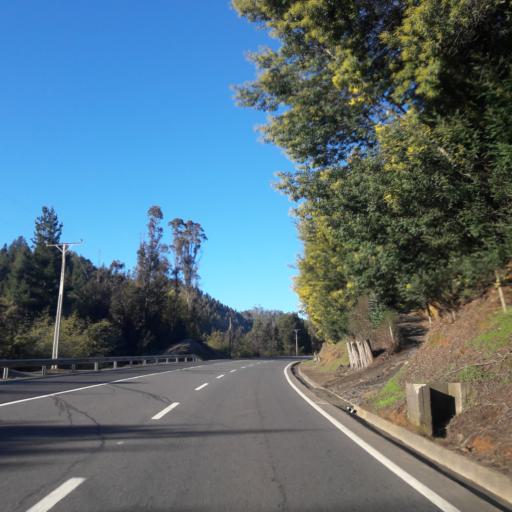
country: CL
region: Biobio
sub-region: Provincia de Biobio
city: La Laja
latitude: -37.2516
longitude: -72.9604
